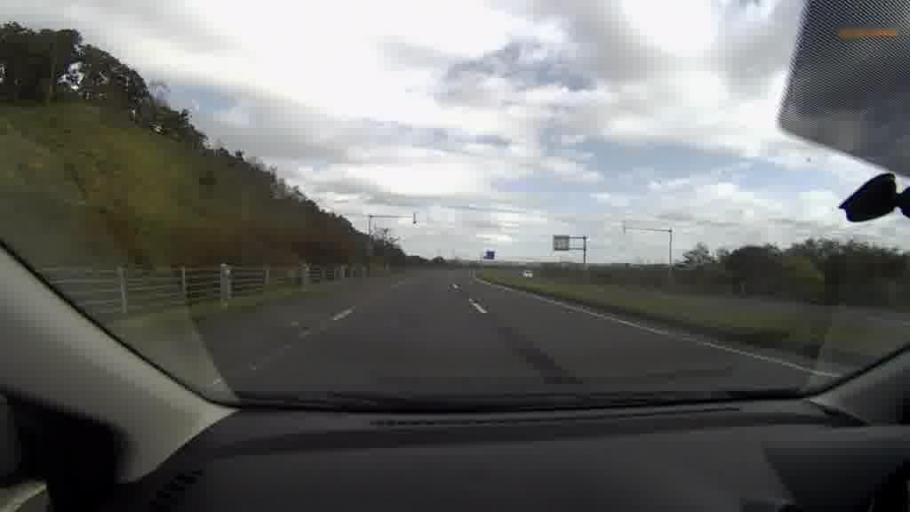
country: JP
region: Hokkaido
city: Kushiro
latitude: 43.0169
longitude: 144.2567
